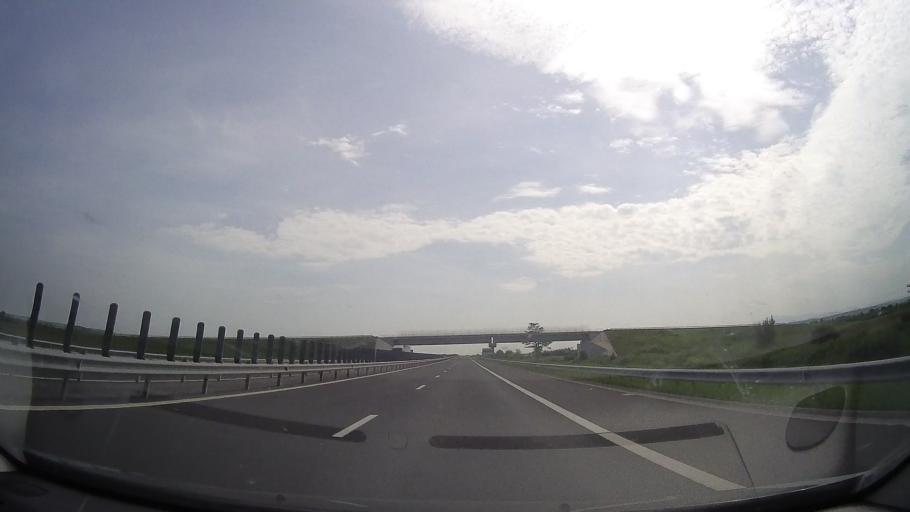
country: RO
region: Timis
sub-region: Comuna Balint
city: Balint
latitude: 45.8035
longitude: 21.8982
